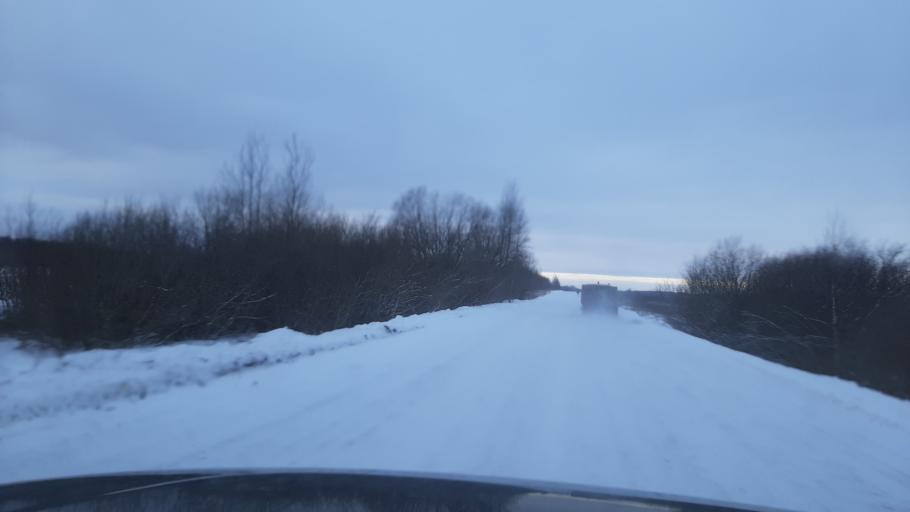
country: RU
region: Kostroma
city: Volgorechensk
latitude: 57.4483
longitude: 41.0086
